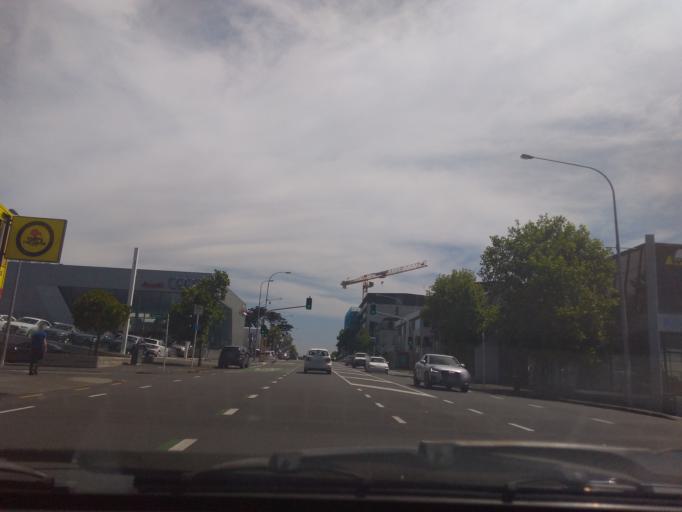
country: NZ
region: Auckland
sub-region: Auckland
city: Auckland
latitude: -36.8625
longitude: 174.7494
